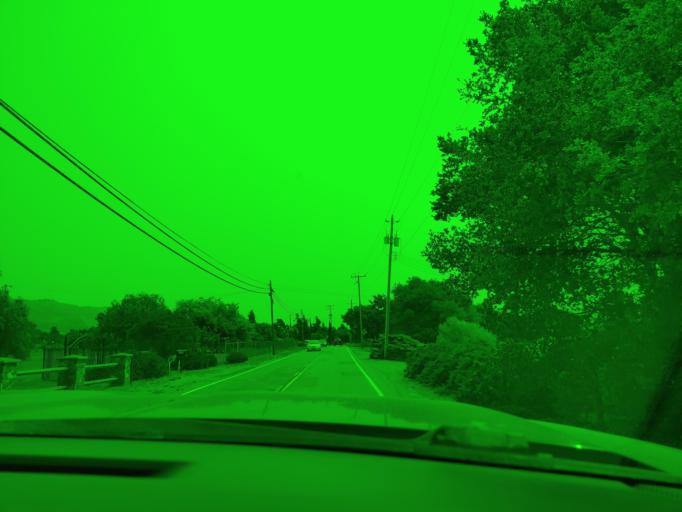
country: US
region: California
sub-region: Santa Cruz County
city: Amesti
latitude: 36.9701
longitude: -121.7696
